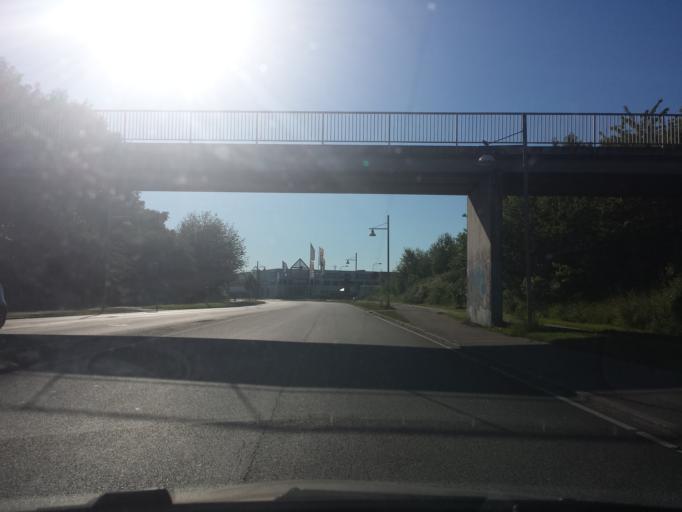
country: DK
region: Capital Region
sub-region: Glostrup Kommune
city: Glostrup
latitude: 55.6843
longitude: 12.3981
